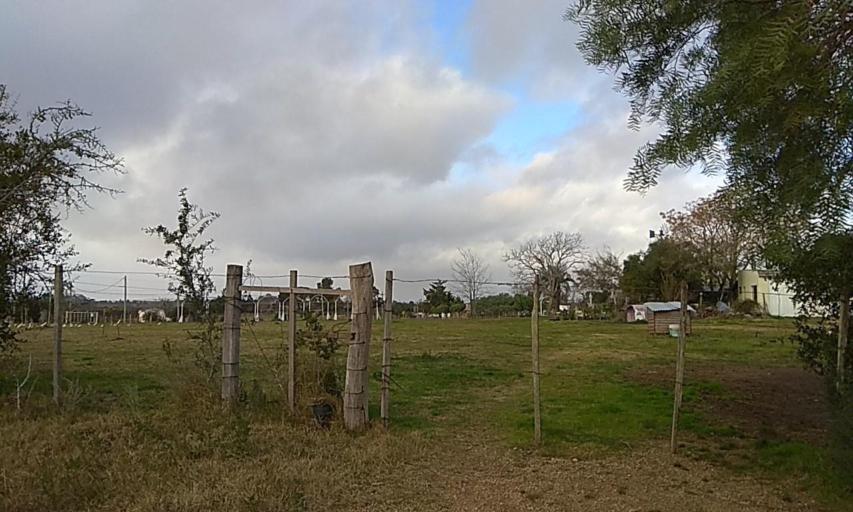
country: UY
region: Florida
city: Florida
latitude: -34.0739
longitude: -56.1990
